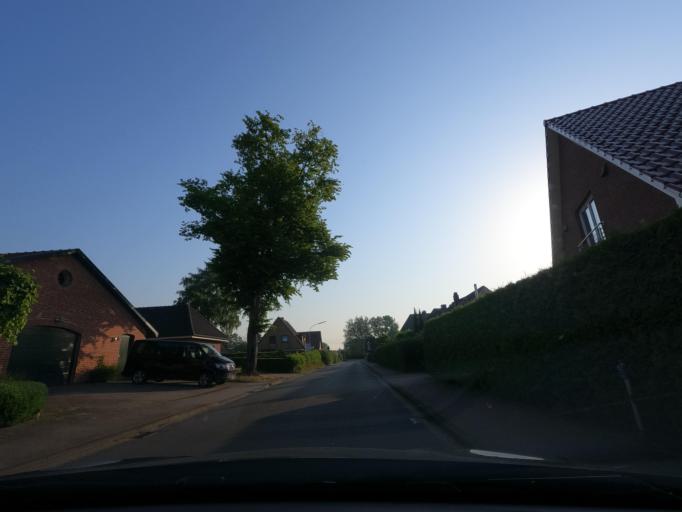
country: DE
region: Schleswig-Holstein
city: Tornesch
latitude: 53.6872
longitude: 9.7303
